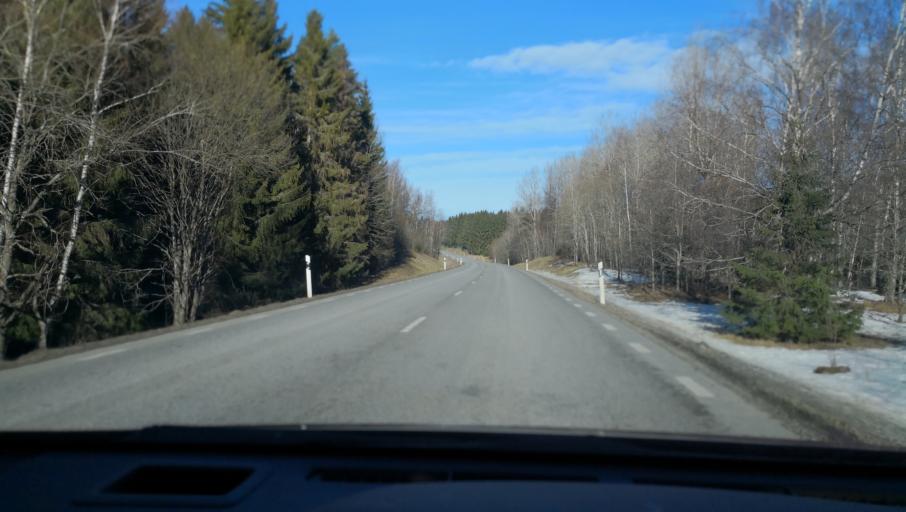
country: SE
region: Uppsala
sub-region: Uppsala Kommun
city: Vattholma
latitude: 60.0260
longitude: 17.7489
